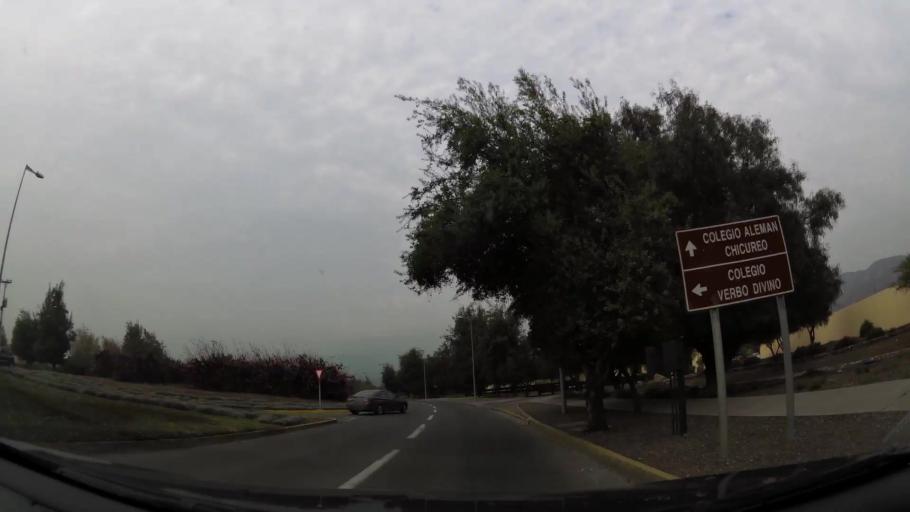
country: CL
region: Santiago Metropolitan
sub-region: Provincia de Chacabuco
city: Chicureo Abajo
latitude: -33.2835
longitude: -70.6437
